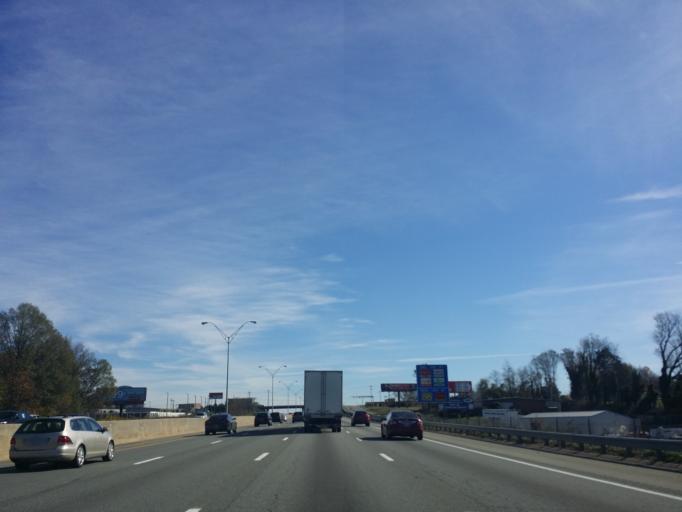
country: US
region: North Carolina
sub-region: Alamance County
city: Graham
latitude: 36.0617
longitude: -79.4109
